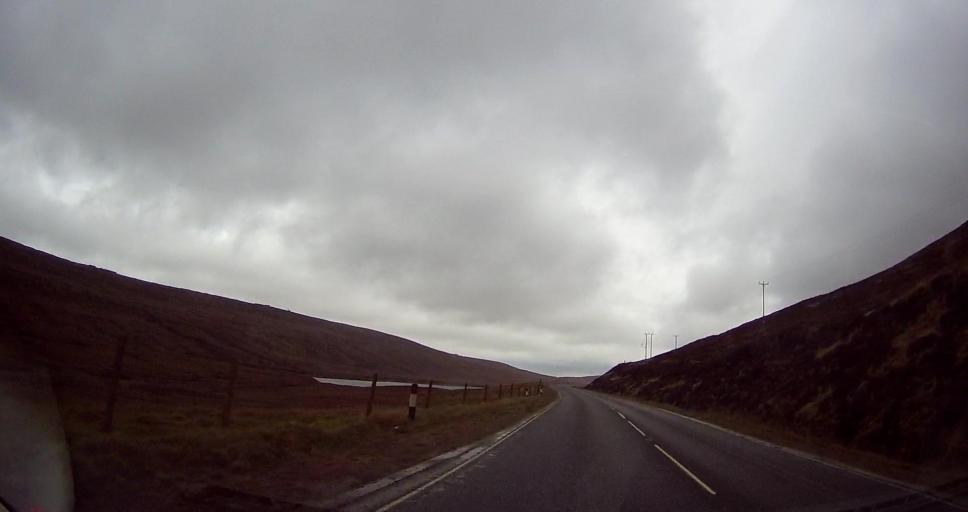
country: GB
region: Scotland
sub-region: Shetland Islands
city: Lerwick
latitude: 60.3092
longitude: -1.2449
